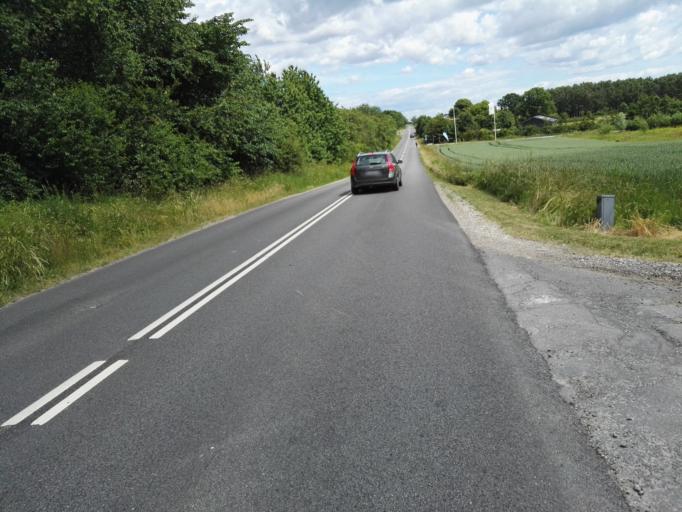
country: DK
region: Capital Region
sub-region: Egedal Kommune
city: Olstykke
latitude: 55.7665
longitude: 12.1593
